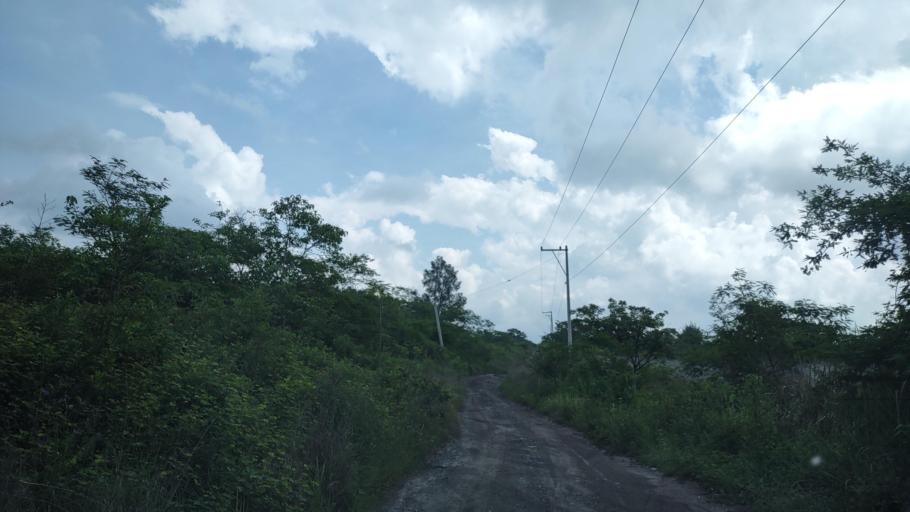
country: MX
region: Veracruz
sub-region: Emiliano Zapata
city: Dos Rios
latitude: 19.4518
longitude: -96.8091
